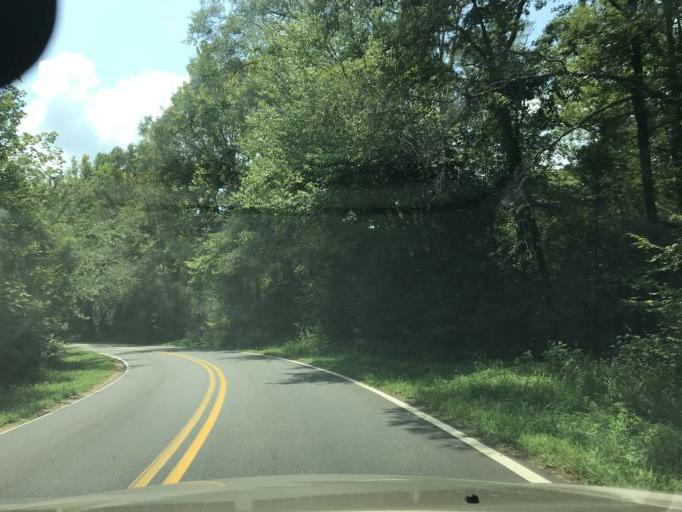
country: US
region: Georgia
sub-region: Forsyth County
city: Cumming
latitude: 34.3129
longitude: -84.2226
